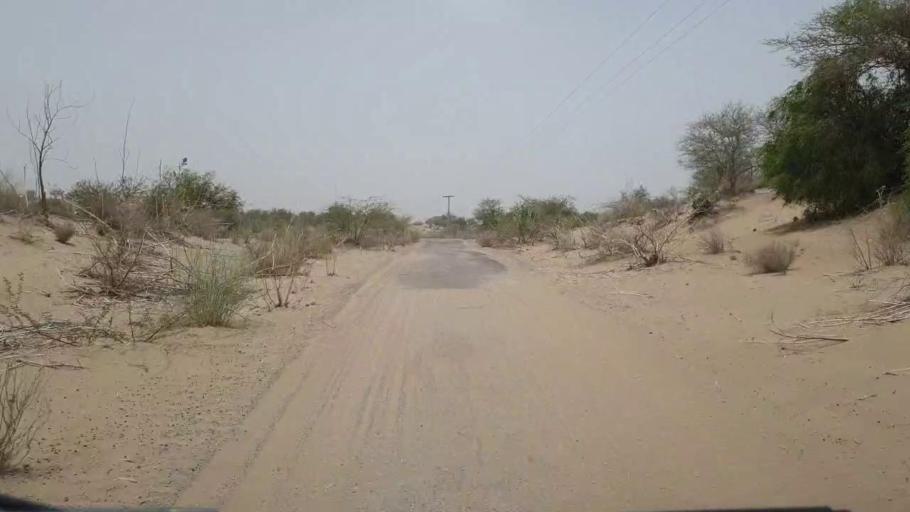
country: PK
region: Sindh
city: Naukot
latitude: 24.7477
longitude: 69.5504
